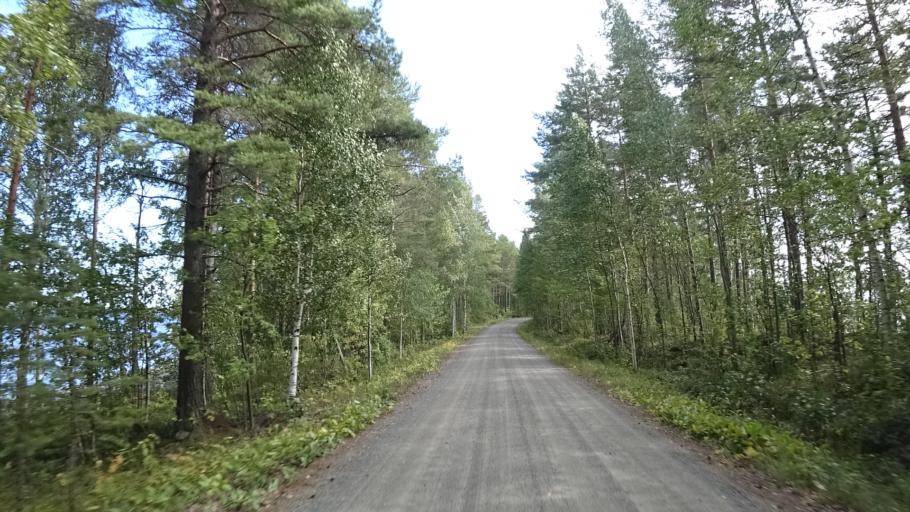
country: FI
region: North Karelia
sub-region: Keski-Karjala
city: Raeaekkylae
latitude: 62.3951
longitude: 29.7668
